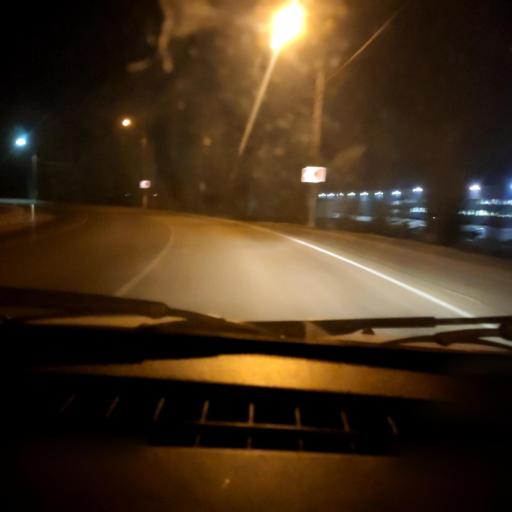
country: RU
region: Voronezj
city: Ramon'
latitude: 51.9299
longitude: 39.2178
